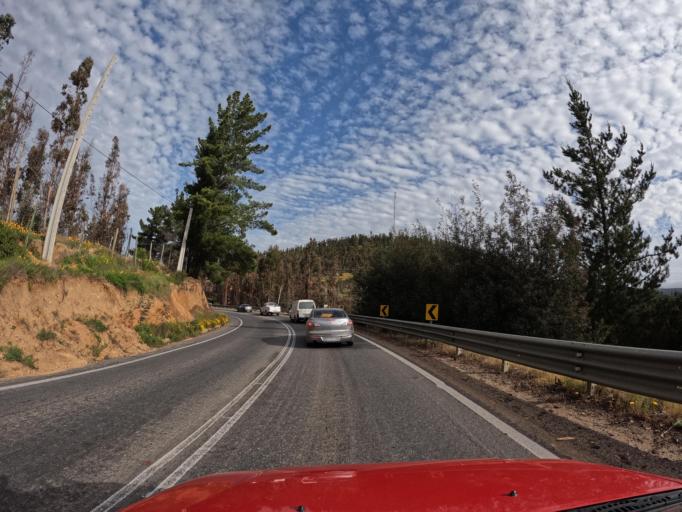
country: CL
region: O'Higgins
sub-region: Provincia de Colchagua
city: Santa Cruz
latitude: -34.2997
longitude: -71.8001
